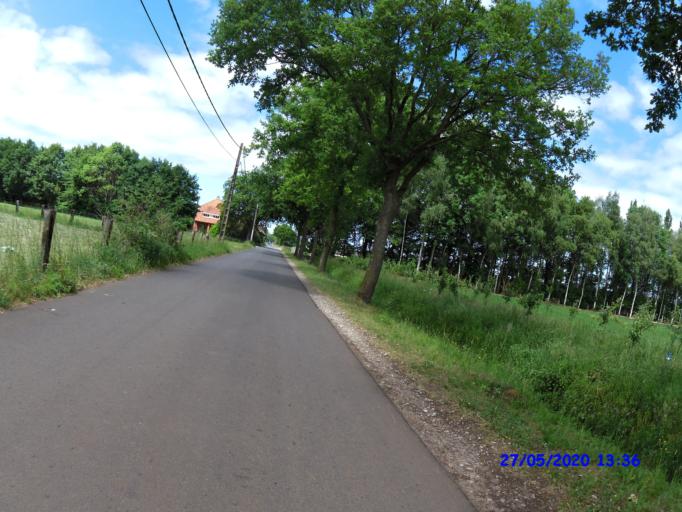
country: BE
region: Flanders
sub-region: Provincie Antwerpen
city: Kasterlee
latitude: 51.2003
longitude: 4.9493
